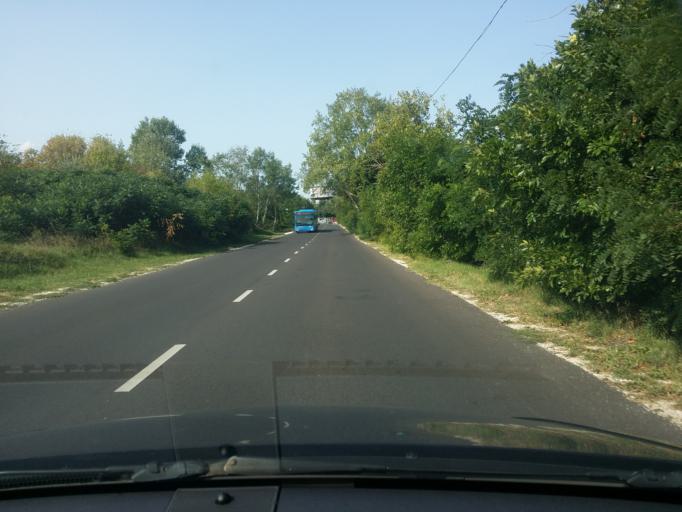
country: HU
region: Budapest
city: Budapest X. keruelet
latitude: 47.4975
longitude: 19.1416
